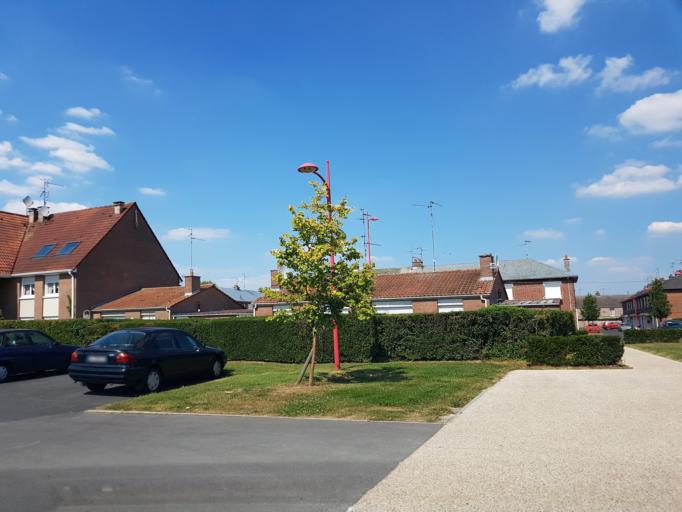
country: FR
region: Nord-Pas-de-Calais
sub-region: Departement du Nord
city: Roeulx
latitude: 50.3079
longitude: 3.3330
